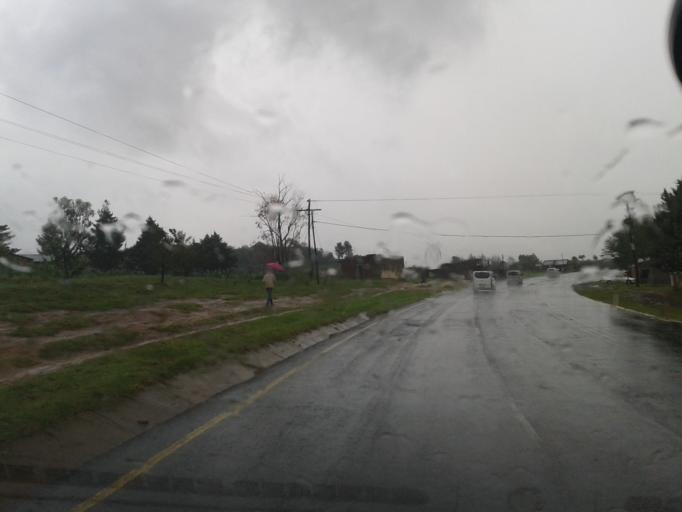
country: LS
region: Maseru
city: Nako
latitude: -29.6433
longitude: 27.4751
